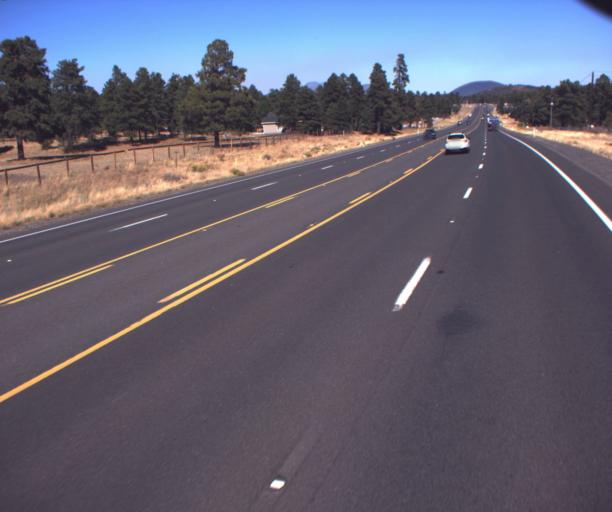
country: US
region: Arizona
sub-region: Coconino County
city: Flagstaff
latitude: 35.2624
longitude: -111.5487
